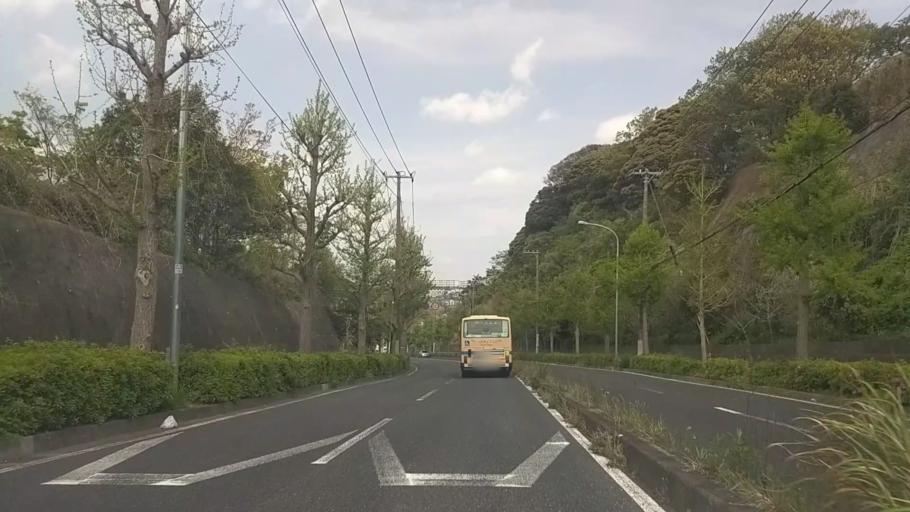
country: JP
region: Kanagawa
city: Yokohama
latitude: 35.3874
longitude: 139.5871
